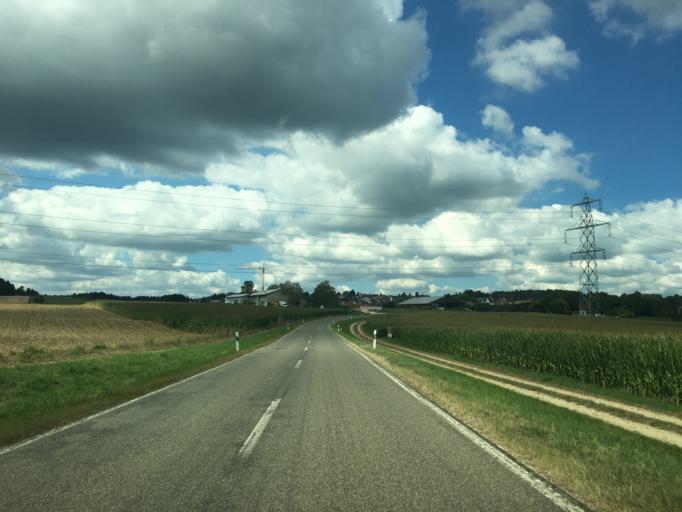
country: DE
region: Baden-Wuerttemberg
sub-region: Tuebingen Region
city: Hayingen
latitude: 48.2711
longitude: 9.4849
